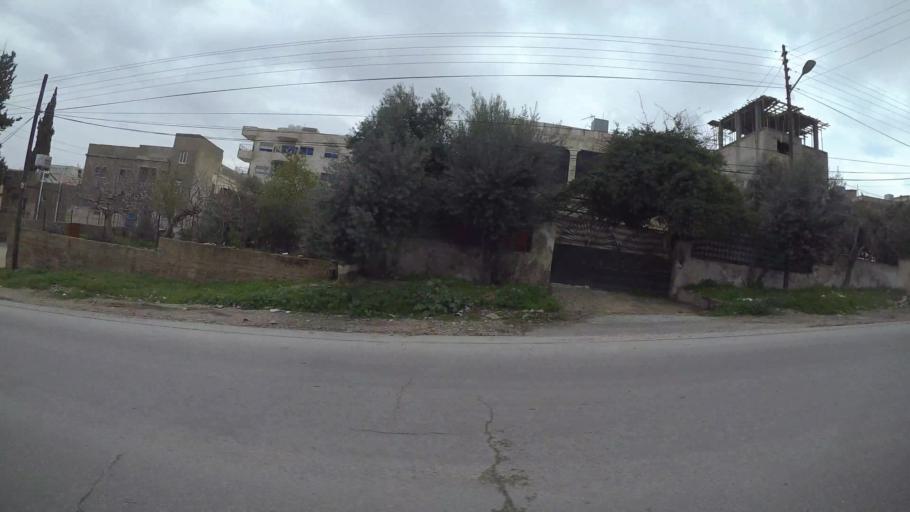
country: JO
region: Amman
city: Al Jubayhah
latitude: 32.0429
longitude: 35.8313
